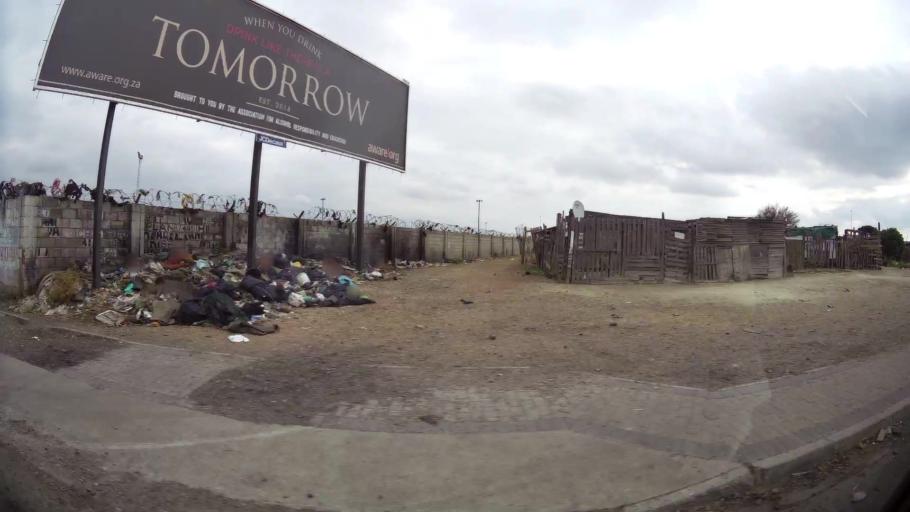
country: ZA
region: Eastern Cape
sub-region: Nelson Mandela Bay Metropolitan Municipality
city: Port Elizabeth
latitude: -33.8827
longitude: 25.5965
